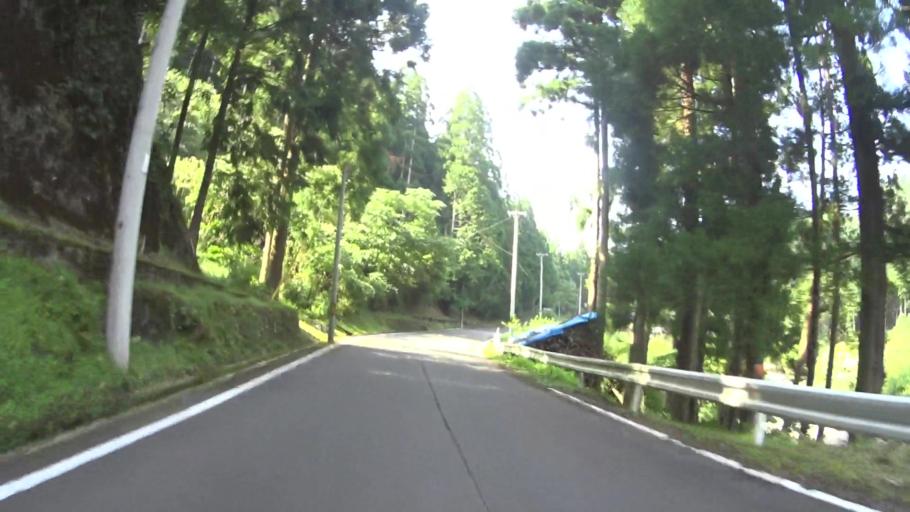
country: JP
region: Fukui
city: Obama
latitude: 35.3061
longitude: 135.6430
